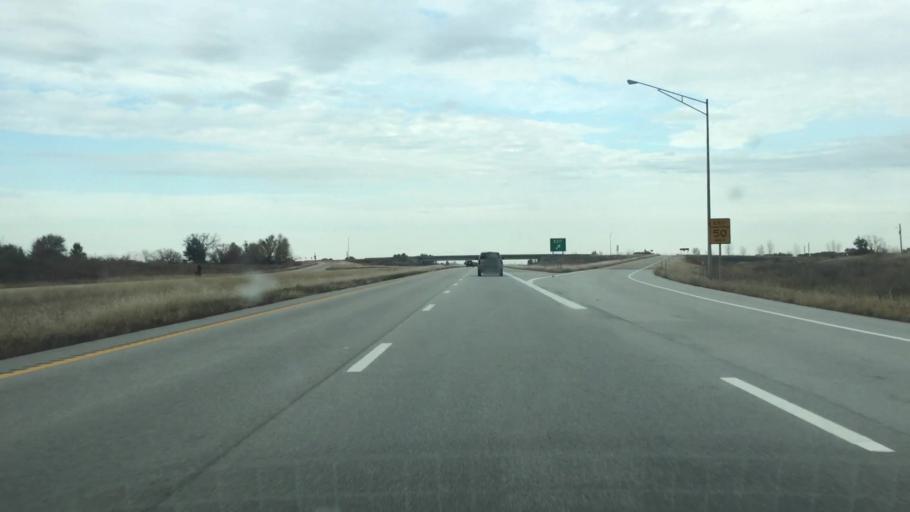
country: US
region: Missouri
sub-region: Henry County
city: Clinton
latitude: 38.2453
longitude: -93.7618
